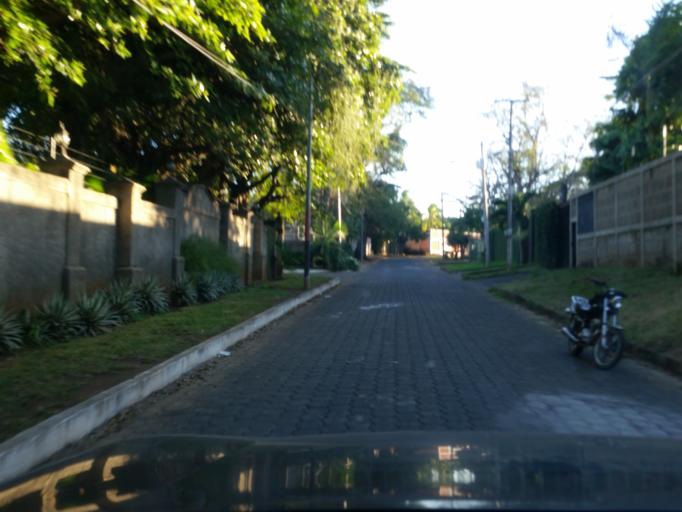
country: NI
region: Managua
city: Managua
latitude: 12.0939
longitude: -86.2297
